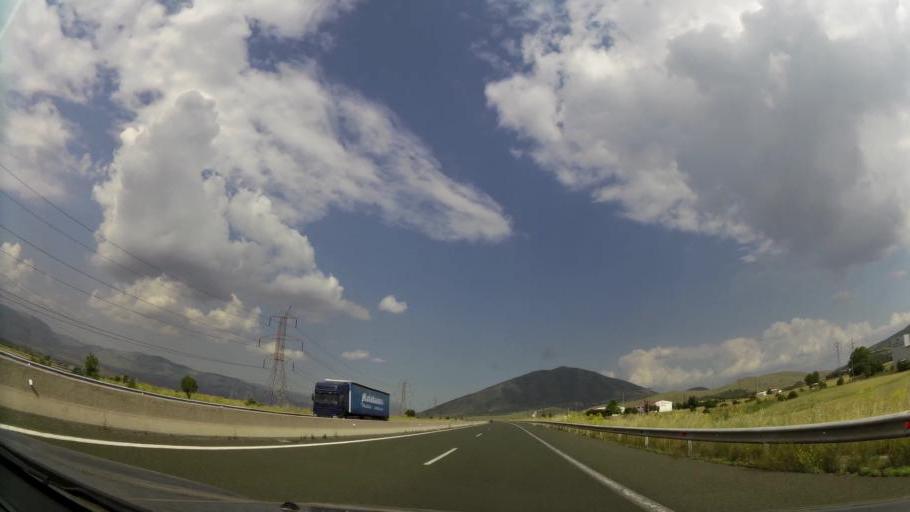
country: GR
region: West Macedonia
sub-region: Nomos Kozanis
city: Koila
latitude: 40.3612
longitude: 21.8419
